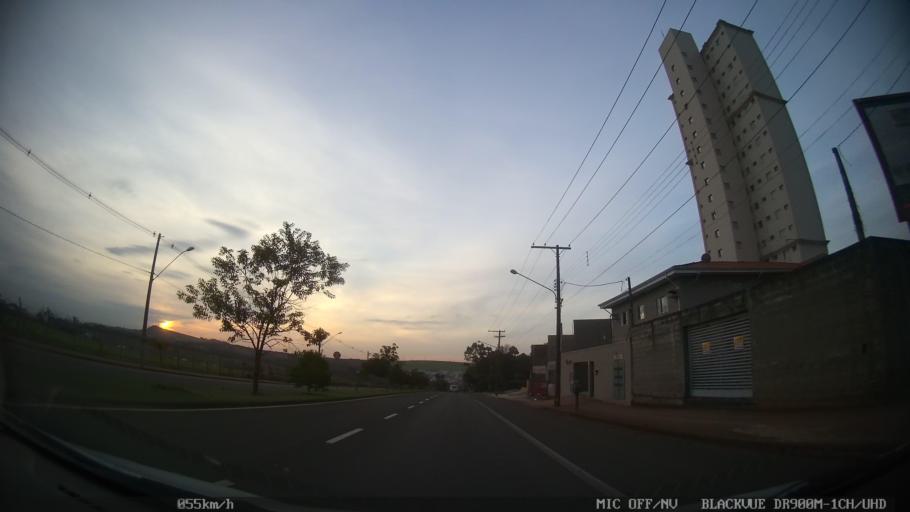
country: BR
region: Sao Paulo
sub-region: Limeira
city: Limeira
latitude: -22.5541
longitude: -47.4256
